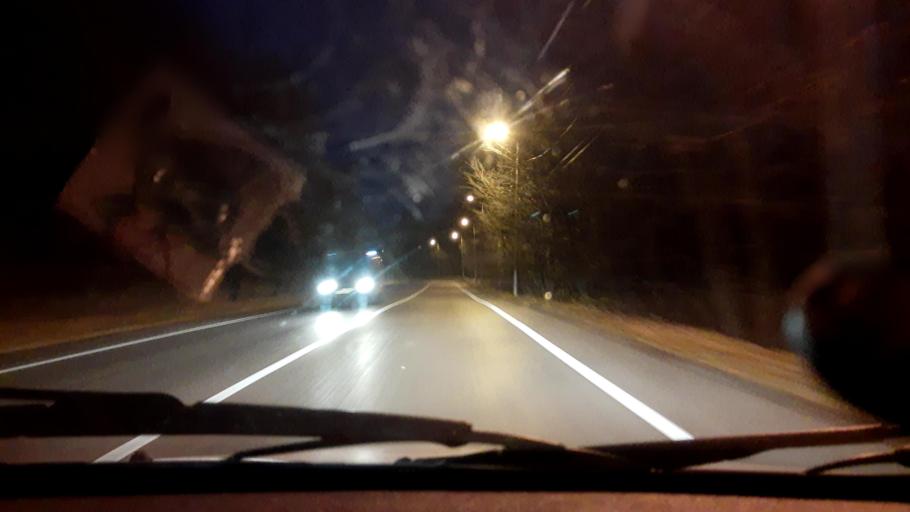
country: RU
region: Bashkortostan
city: Ufa
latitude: 54.8754
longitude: 56.0618
